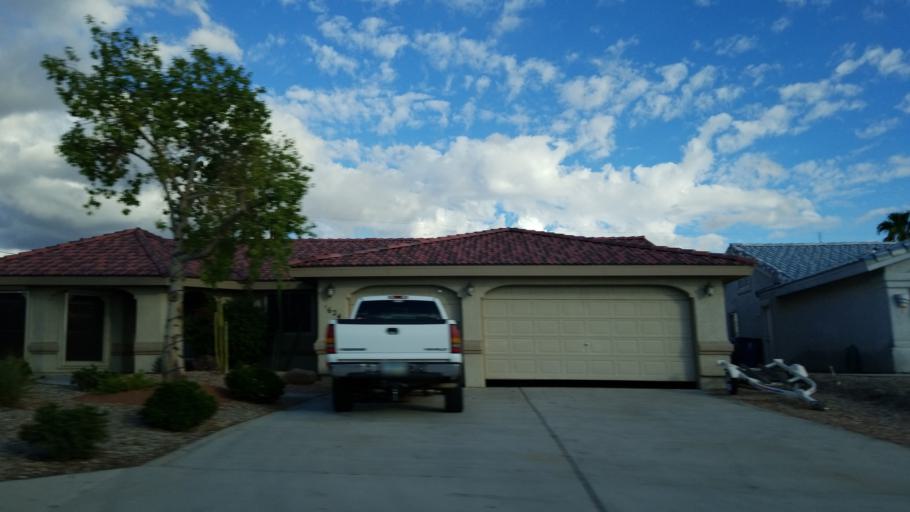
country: US
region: Arizona
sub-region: Mohave County
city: Lake Havasu City
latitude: 34.4575
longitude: -114.2594
